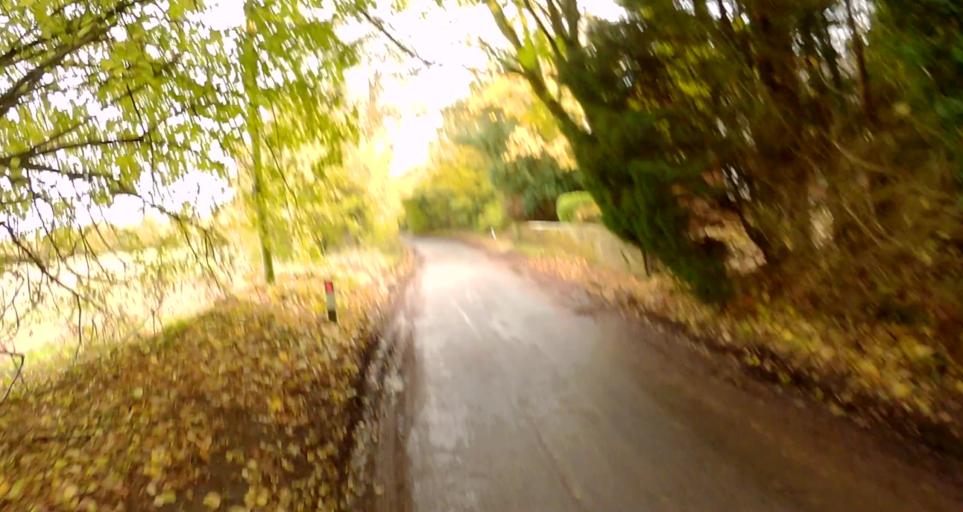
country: GB
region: England
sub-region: Hampshire
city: Long Sutton
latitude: 51.2193
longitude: -0.9364
